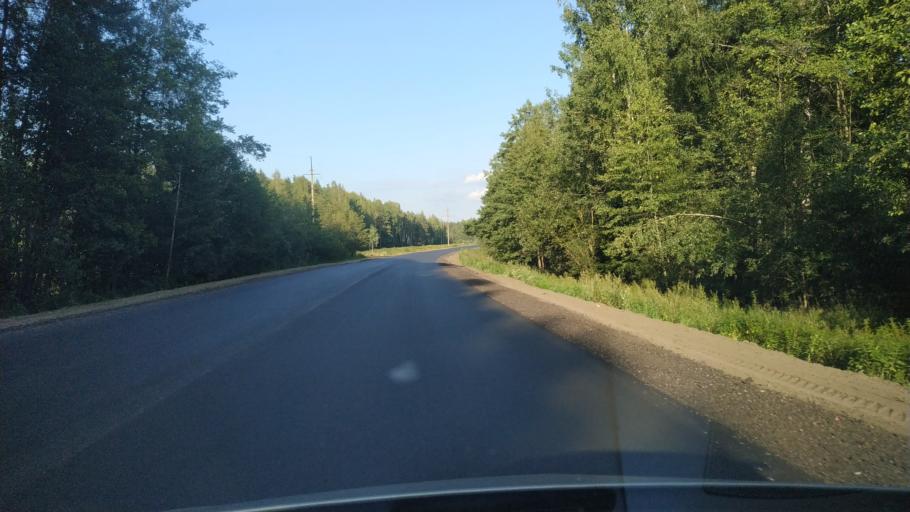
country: RU
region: Moskovskaya
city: Kerva
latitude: 55.5675
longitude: 39.6581
